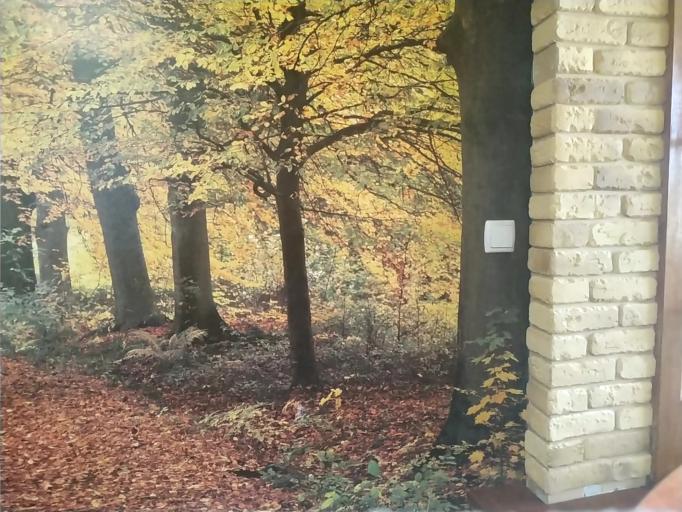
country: RU
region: Tverskaya
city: Krasnomayskiy
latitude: 57.7064
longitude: 34.4887
